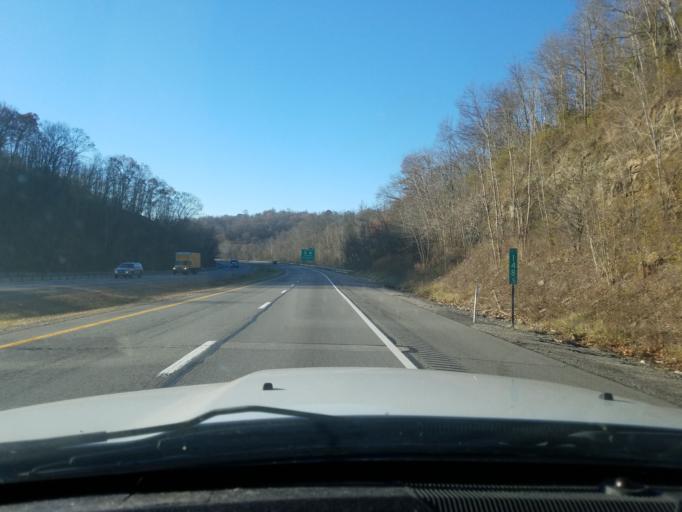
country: US
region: West Virginia
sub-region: Jackson County
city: Ravenswood
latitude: 38.9556
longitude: -81.7032
